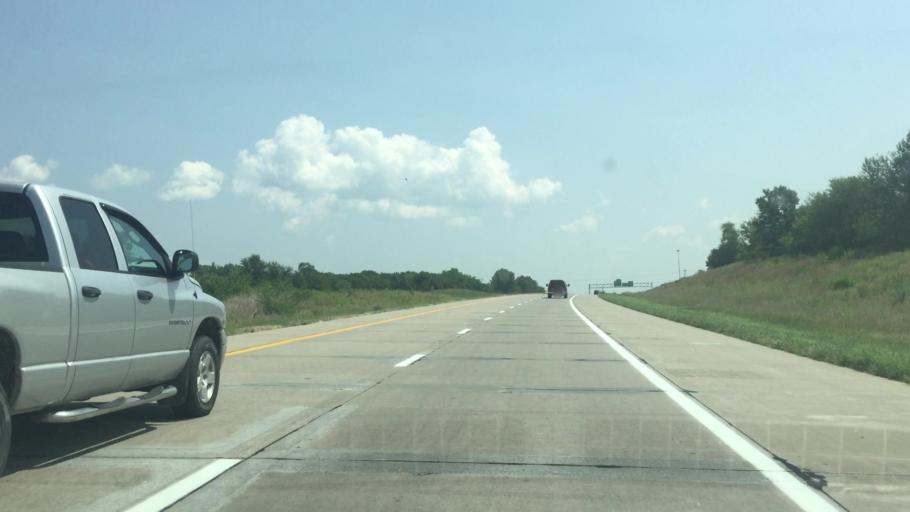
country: US
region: Kansas
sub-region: Franklin County
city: Ottawa
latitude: 38.5682
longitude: -95.2964
